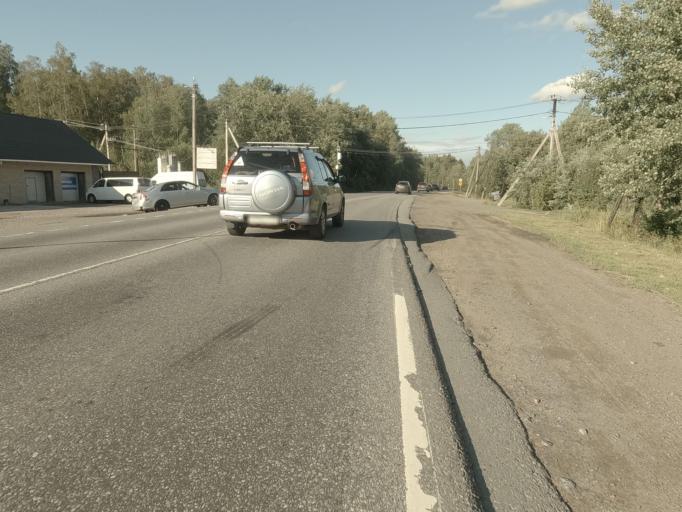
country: RU
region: Leningrad
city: Kirovsk
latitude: 59.9270
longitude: 30.9774
